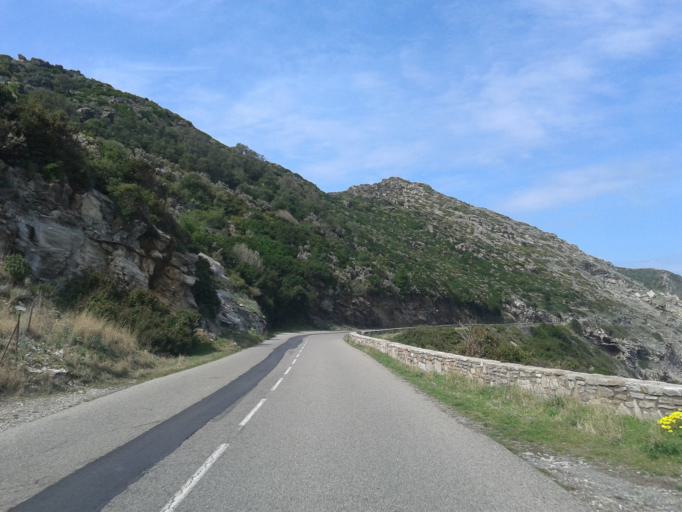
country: FR
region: Corsica
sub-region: Departement de la Haute-Corse
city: Brando
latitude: 42.8181
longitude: 9.4876
